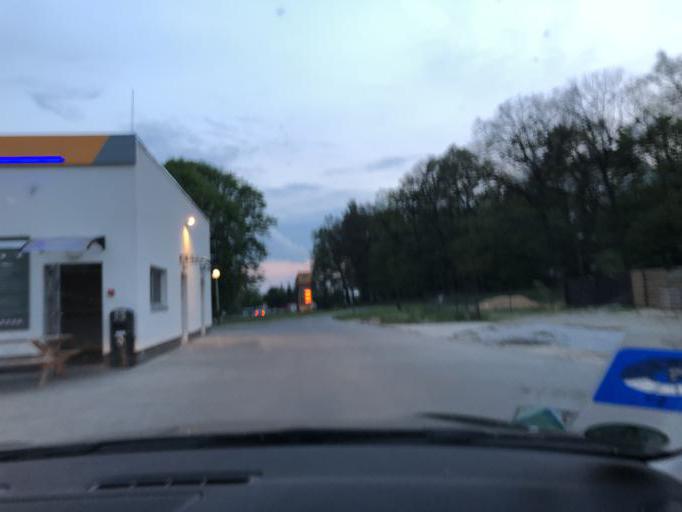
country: PL
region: Lubusz
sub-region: Powiat zarski
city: Leknica
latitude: 51.5442
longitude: 14.7476
